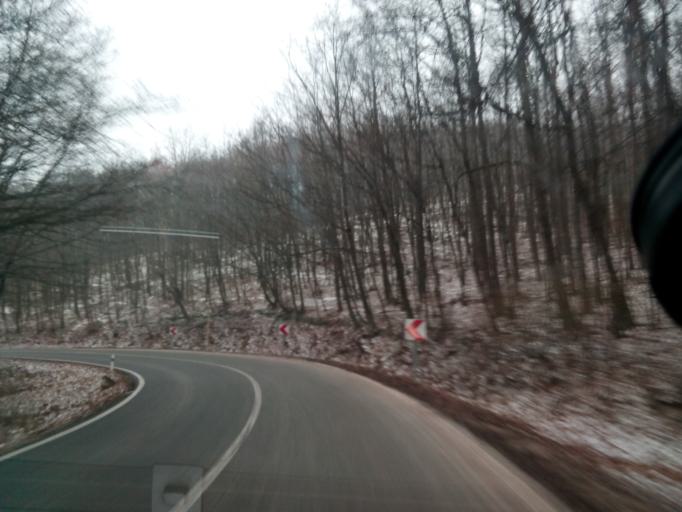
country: SK
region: Kosicky
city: Kosice
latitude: 48.7121
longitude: 21.1937
